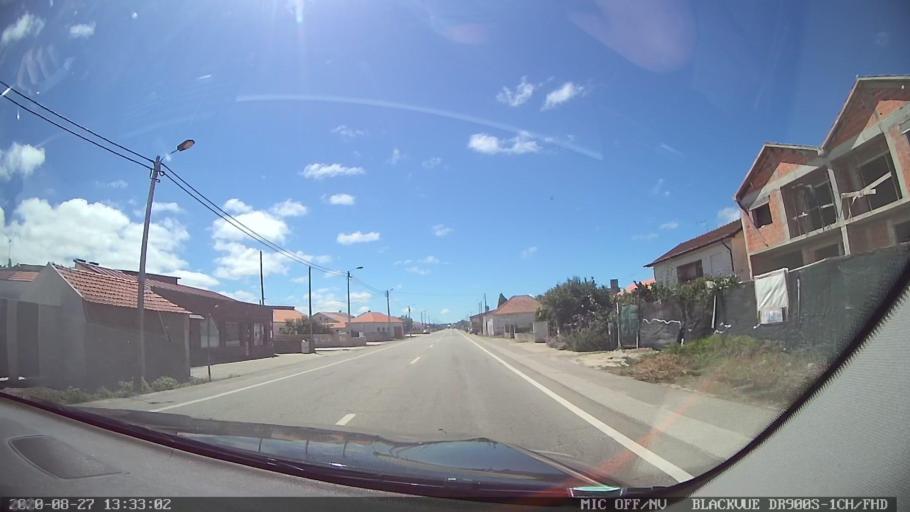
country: PT
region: Coimbra
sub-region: Mira
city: Mira
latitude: 40.4822
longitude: -8.6909
